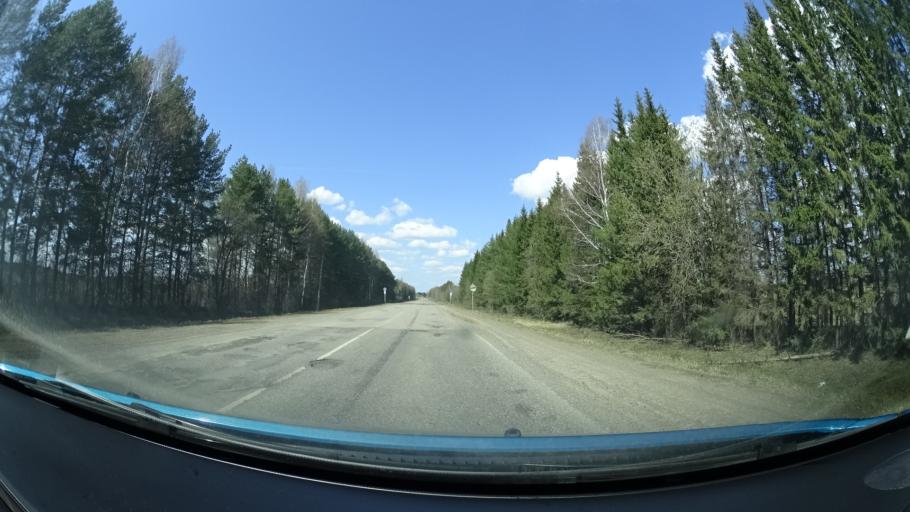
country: RU
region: Perm
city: Osa
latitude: 57.3168
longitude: 55.6230
